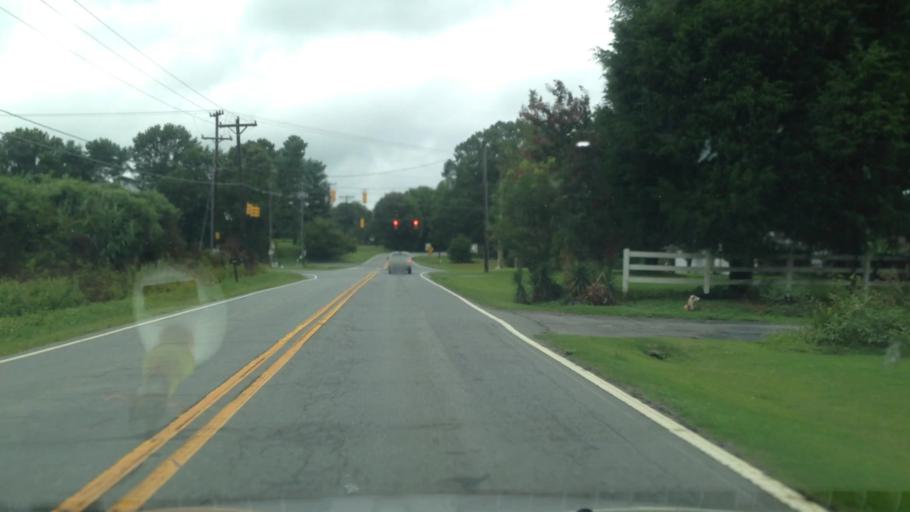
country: US
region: North Carolina
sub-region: Guilford County
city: Stokesdale
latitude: 36.2169
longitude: -80.0571
